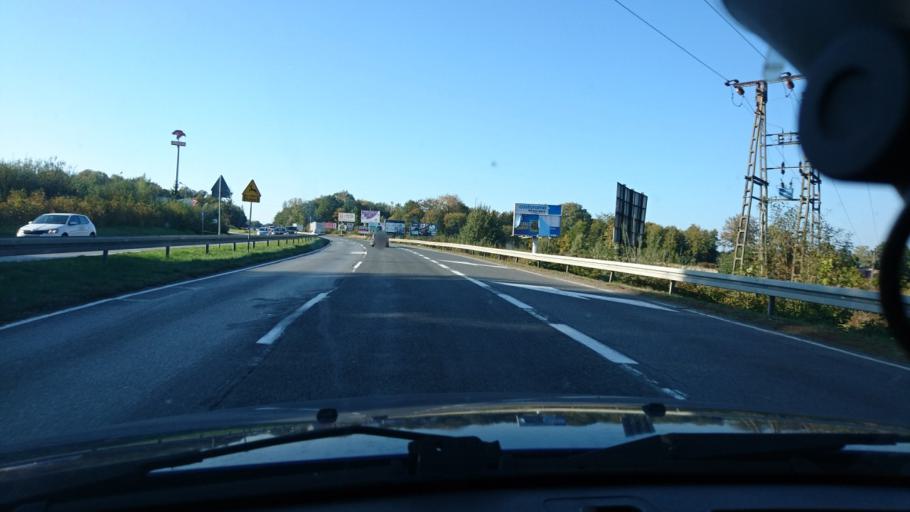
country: PL
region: Silesian Voivodeship
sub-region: Bielsko-Biala
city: Bielsko-Biala
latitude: 49.8586
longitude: 19.0252
